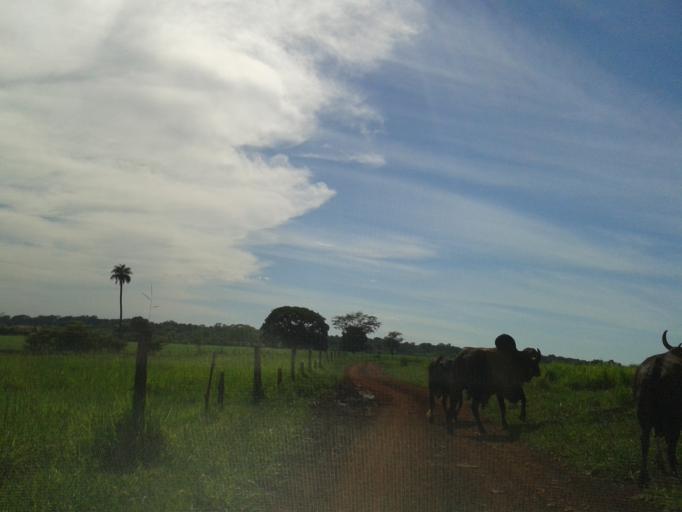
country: BR
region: Minas Gerais
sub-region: Capinopolis
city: Capinopolis
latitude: -18.6255
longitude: -49.7369
